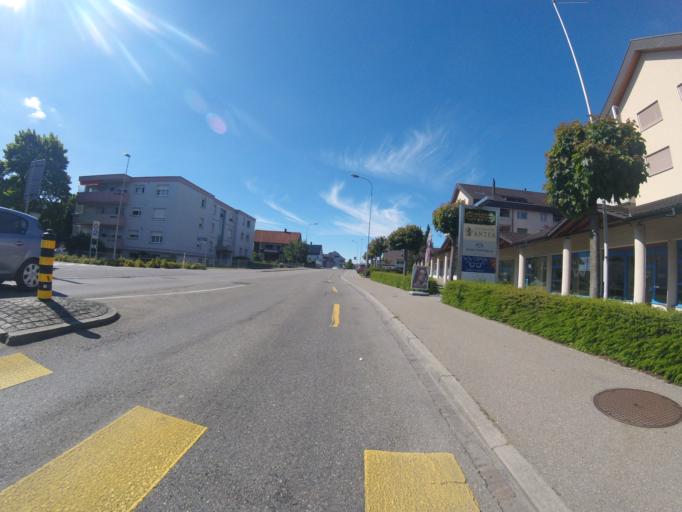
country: CH
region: Saint Gallen
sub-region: Wahlkreis Wil
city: Wil
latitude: 47.4466
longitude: 9.0507
